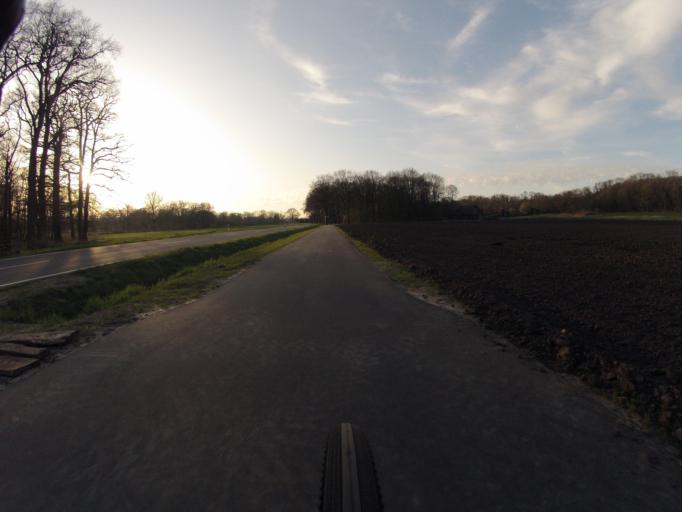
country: DE
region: North Rhine-Westphalia
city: Ibbenburen
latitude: 52.2288
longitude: 7.7160
